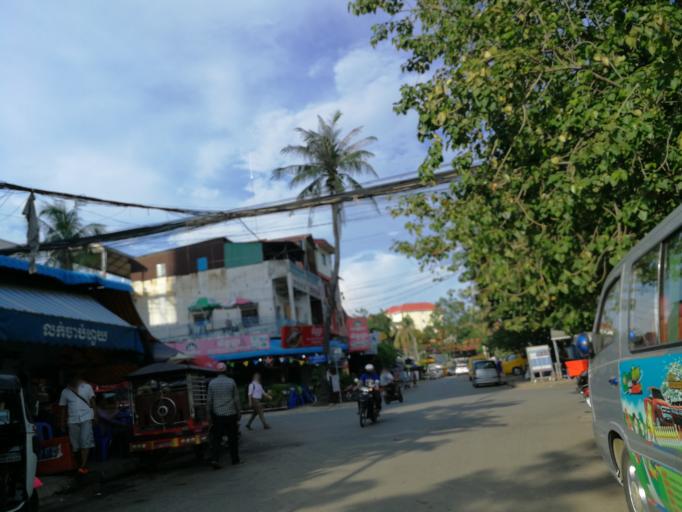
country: KH
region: Phnom Penh
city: Phnom Penh
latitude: 11.5799
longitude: 104.9192
